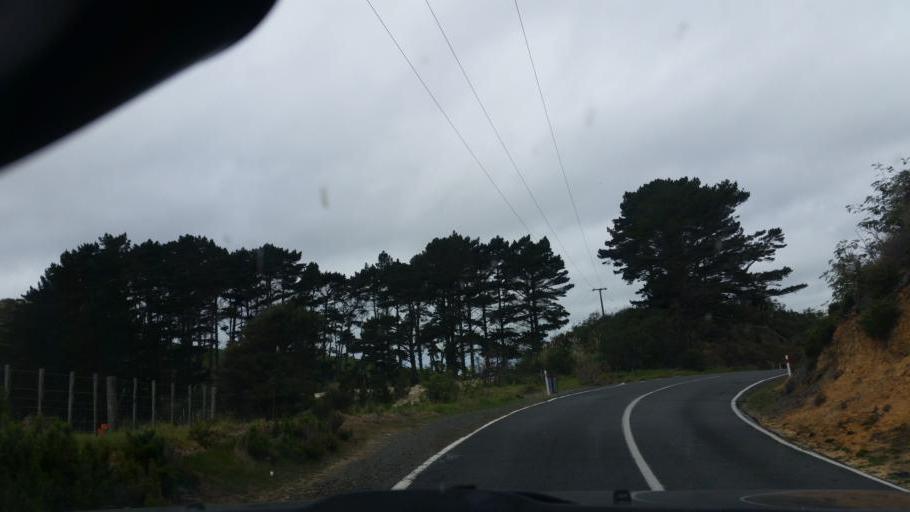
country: NZ
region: Northland
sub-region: Kaipara District
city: Dargaville
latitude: -35.8218
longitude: 173.6872
